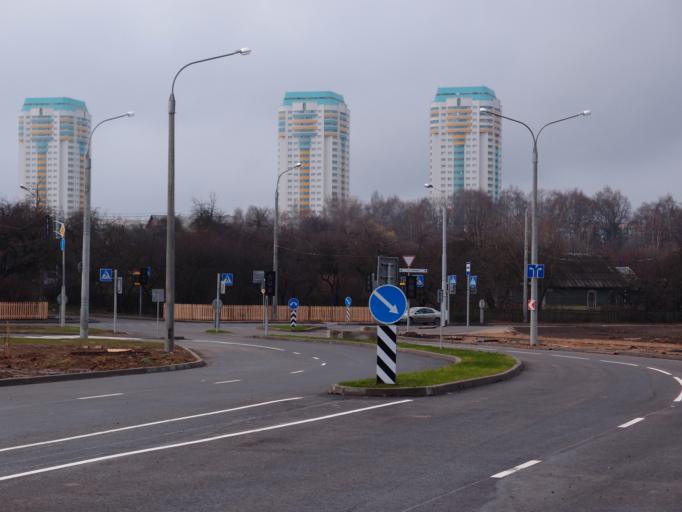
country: BY
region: Minsk
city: Syenitsa
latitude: 53.8653
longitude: 27.4978
